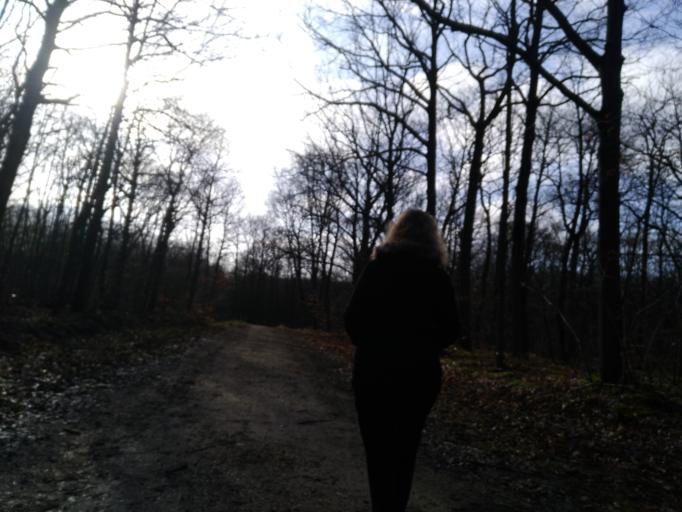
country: FR
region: Ile-de-France
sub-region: Departement des Yvelines
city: Plaisir
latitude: 48.8042
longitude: 1.9387
